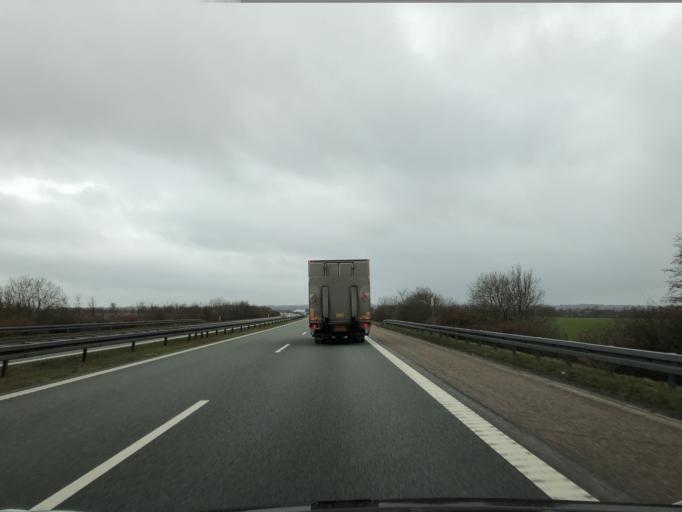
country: DK
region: North Denmark
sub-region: Bronderslev Kommune
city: Hjallerup
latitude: 57.1452
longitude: 10.1072
